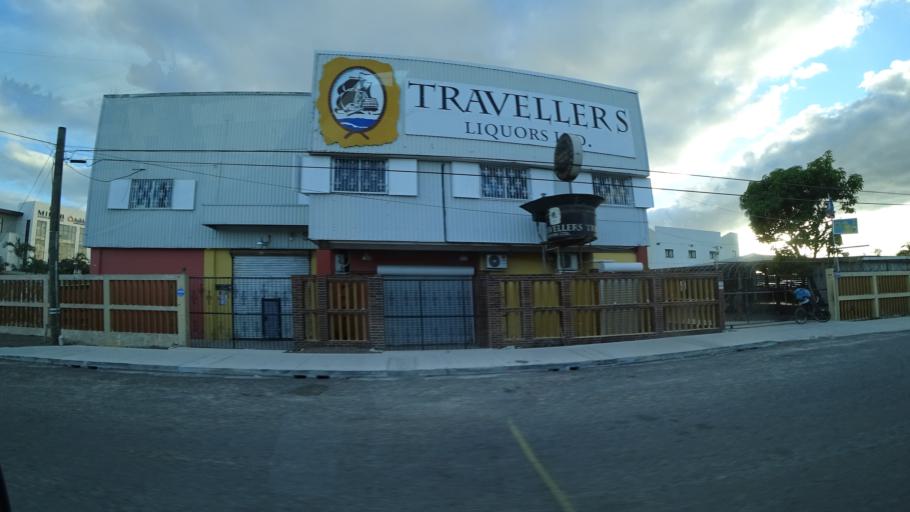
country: BZ
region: Belize
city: Belize City
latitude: 17.5113
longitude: -88.2144
